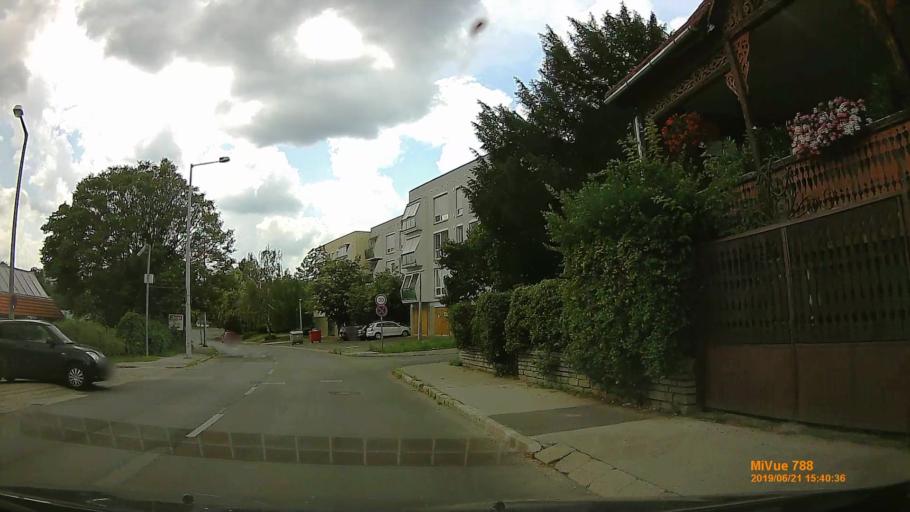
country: HU
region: Baranya
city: Pecs
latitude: 46.0826
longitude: 18.2119
